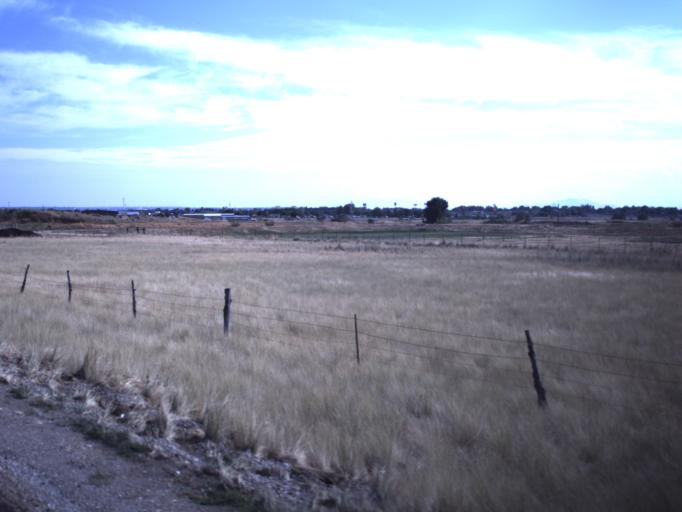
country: US
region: Utah
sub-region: Weber County
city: Pleasant View
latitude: 41.3224
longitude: -112.0177
